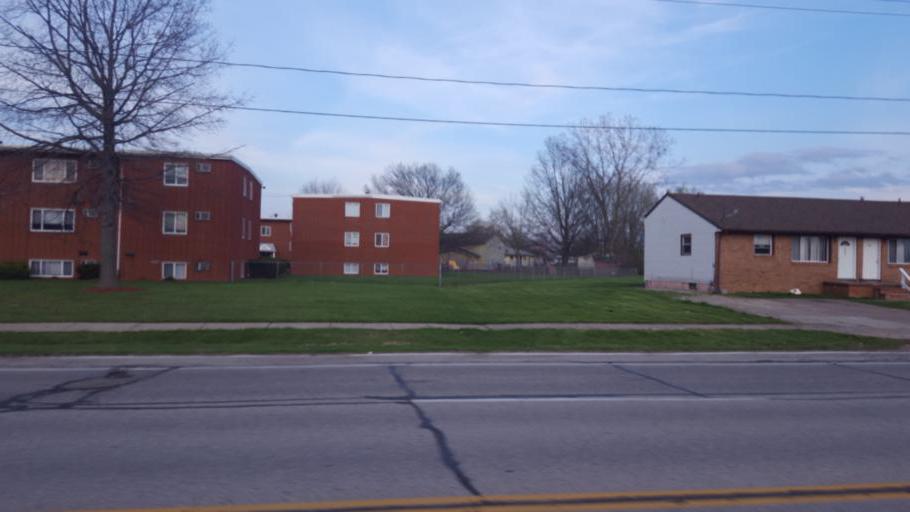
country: US
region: Ohio
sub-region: Lorain County
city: Lorain
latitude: 41.4449
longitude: -82.2025
